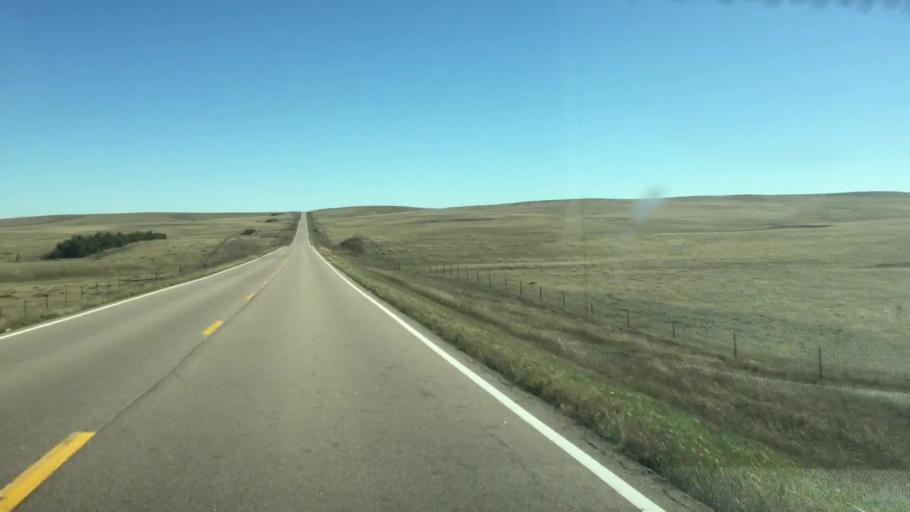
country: US
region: Colorado
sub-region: Lincoln County
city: Limon
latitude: 39.2782
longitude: -103.9975
